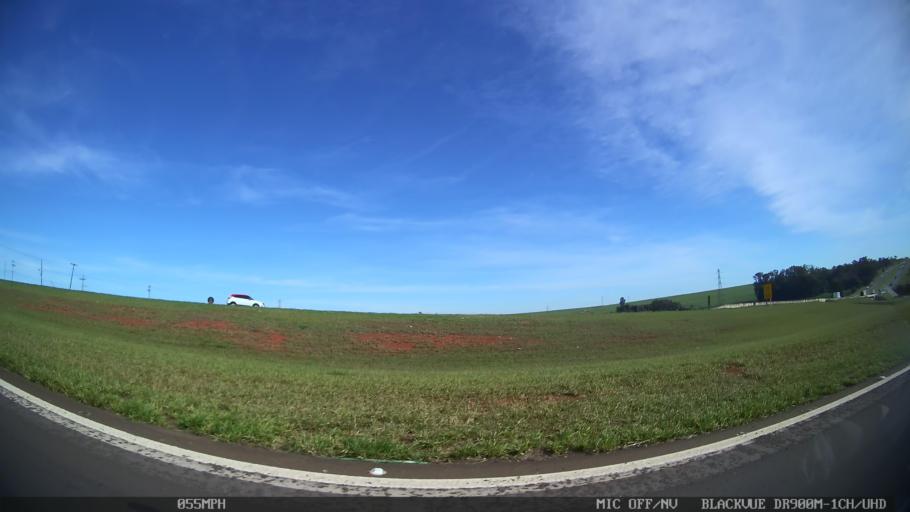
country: BR
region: Sao Paulo
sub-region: Araras
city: Araras
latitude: -22.3973
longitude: -47.3897
